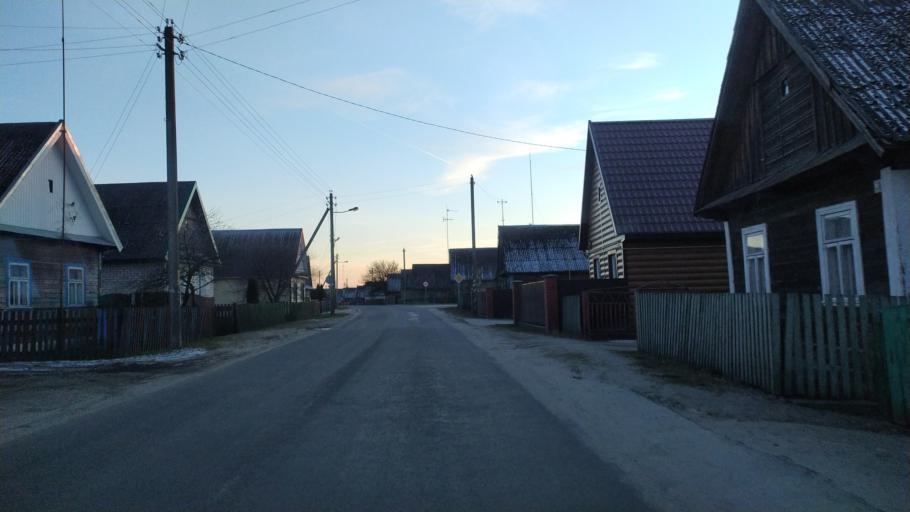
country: BY
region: Brest
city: Pruzhany
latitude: 52.5522
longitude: 24.2115
